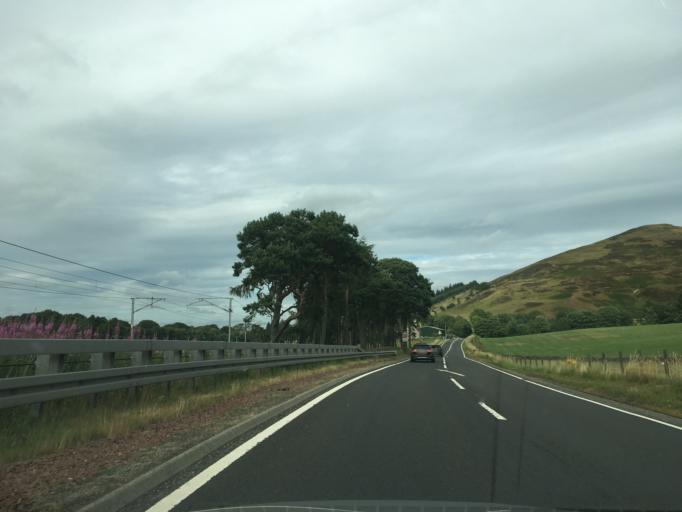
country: GB
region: Scotland
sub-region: South Lanarkshire
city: Biggar
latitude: 55.5476
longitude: -3.6469
